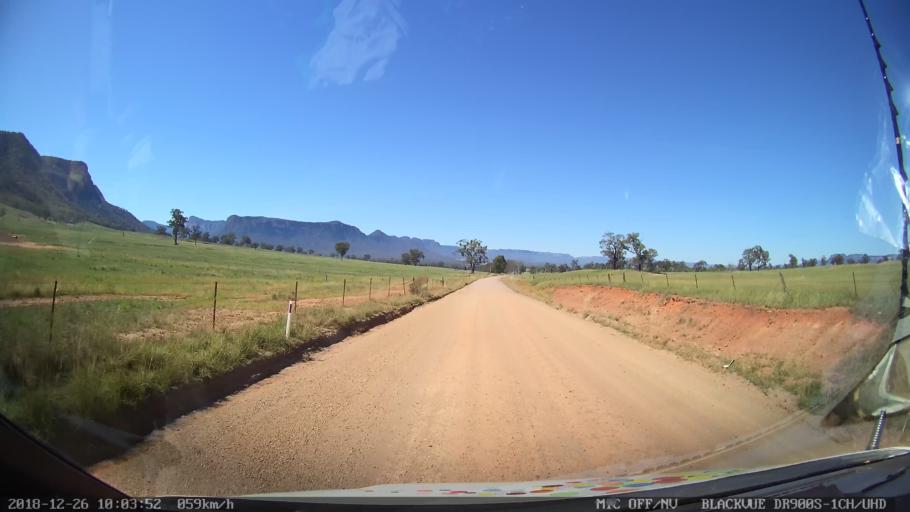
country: AU
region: New South Wales
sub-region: Mid-Western Regional
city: Kandos
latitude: -33.0654
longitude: 150.2166
